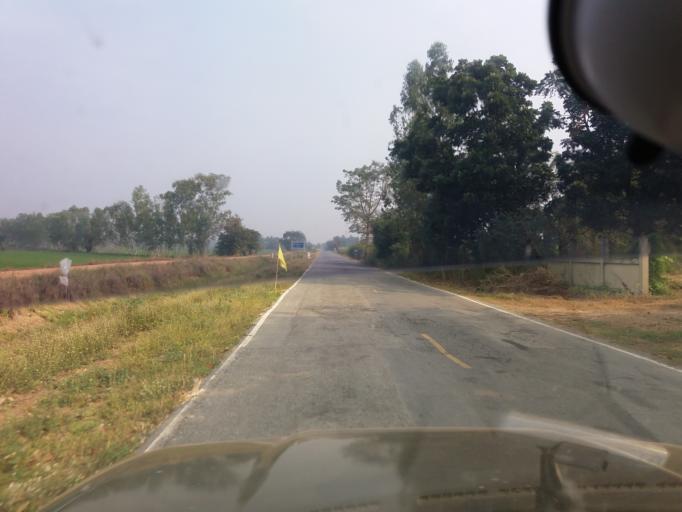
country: TH
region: Suphan Buri
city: Doem Bang Nang Buat
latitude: 14.8646
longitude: 100.1687
